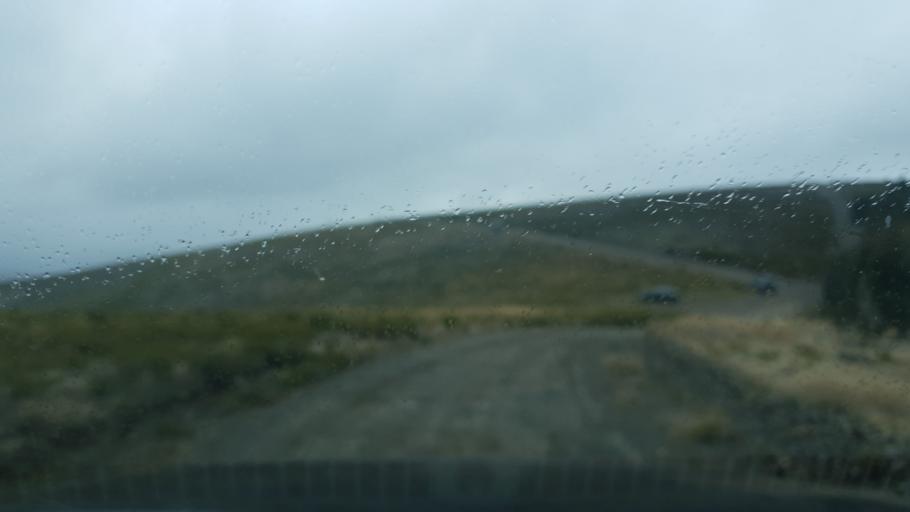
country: PT
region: Viseu
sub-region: Sao Pedro do Sul
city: Sao Pedro do Sul
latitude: 40.8536
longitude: -8.1052
